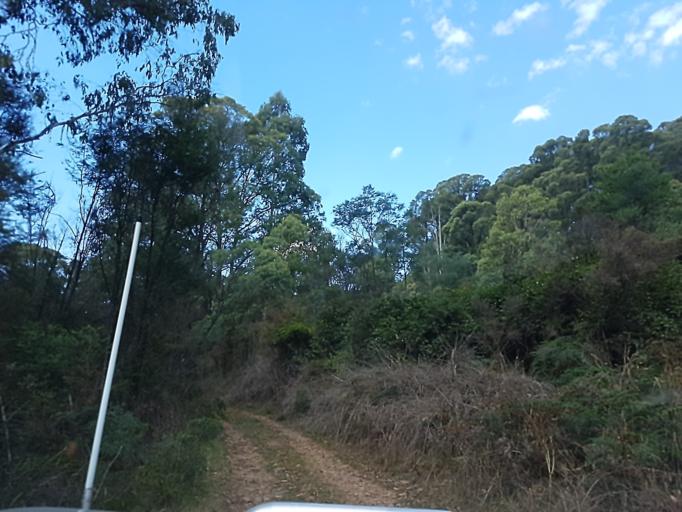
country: AU
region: Victoria
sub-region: Alpine
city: Mount Beauty
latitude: -36.9105
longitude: 147.0485
